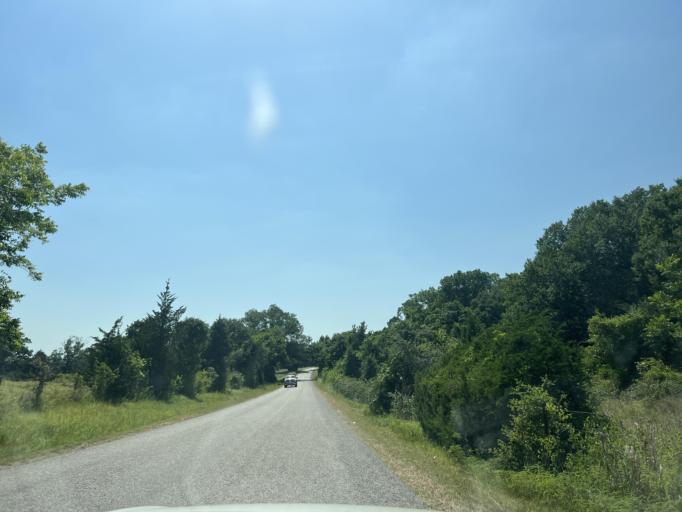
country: US
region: Texas
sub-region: Washington County
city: Brenham
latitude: 30.1537
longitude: -96.4830
